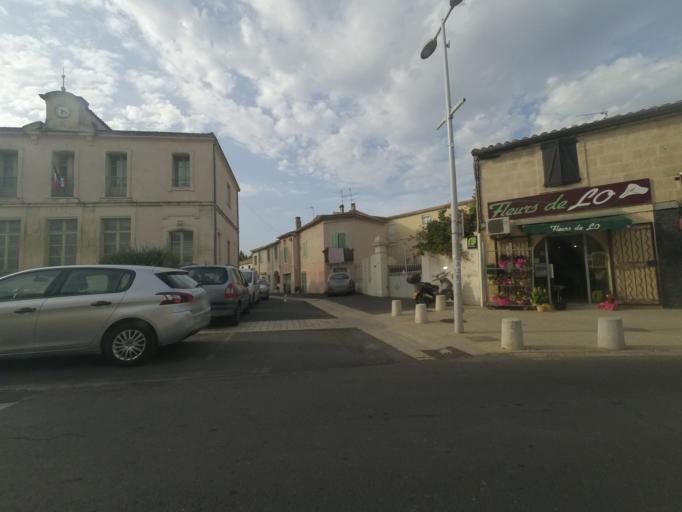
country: FR
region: Languedoc-Roussillon
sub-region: Departement de l'Herault
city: Restinclieres
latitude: 43.7238
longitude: 4.0386
